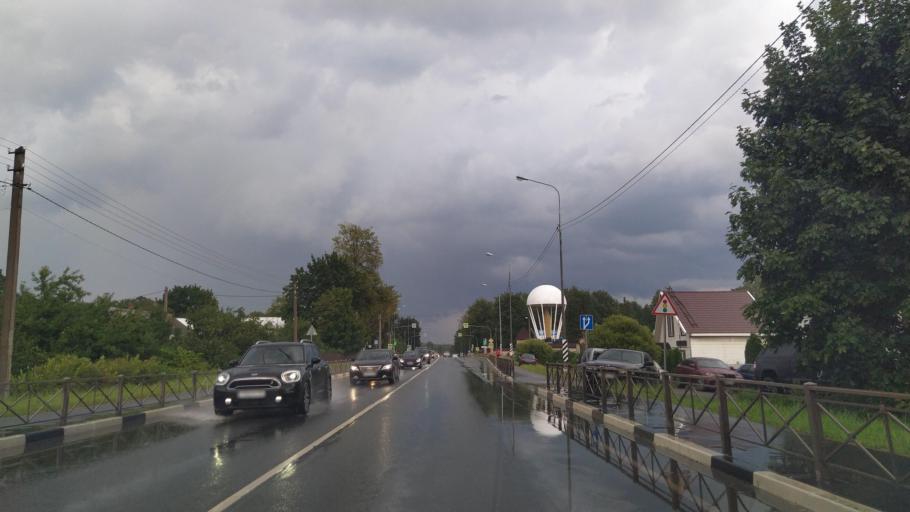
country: RU
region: Pskov
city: Pskov
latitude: 57.7471
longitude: 28.3730
